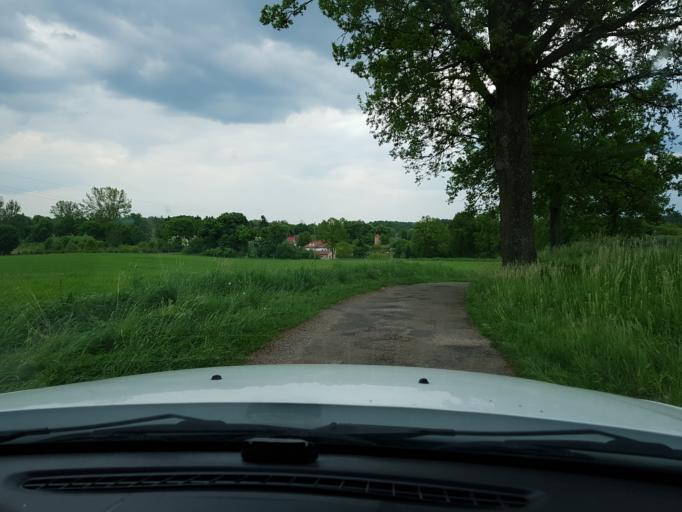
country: PL
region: West Pomeranian Voivodeship
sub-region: Powiat drawski
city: Drawsko Pomorskie
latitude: 53.5212
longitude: 15.7506
